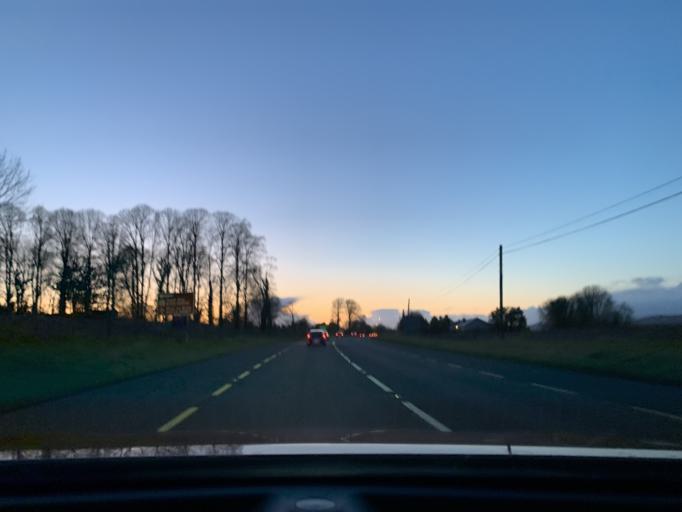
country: IE
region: Connaught
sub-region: Roscommon
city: Boyle
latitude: 53.9693
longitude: -8.2565
